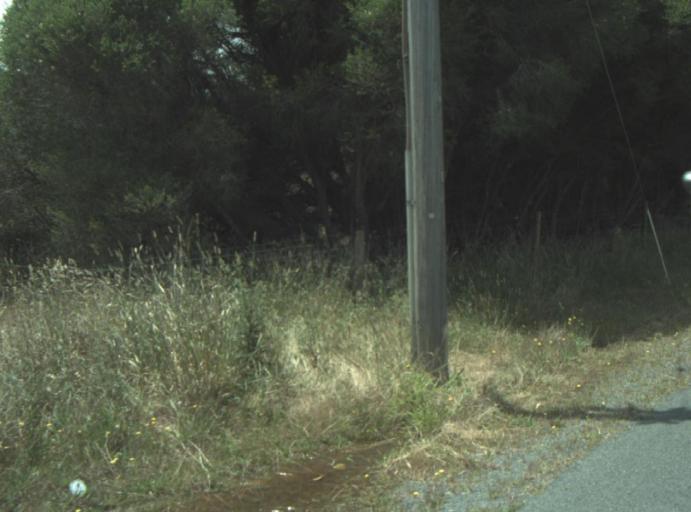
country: AU
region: Victoria
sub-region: Greater Geelong
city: Wandana Heights
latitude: -38.2452
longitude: 144.3036
